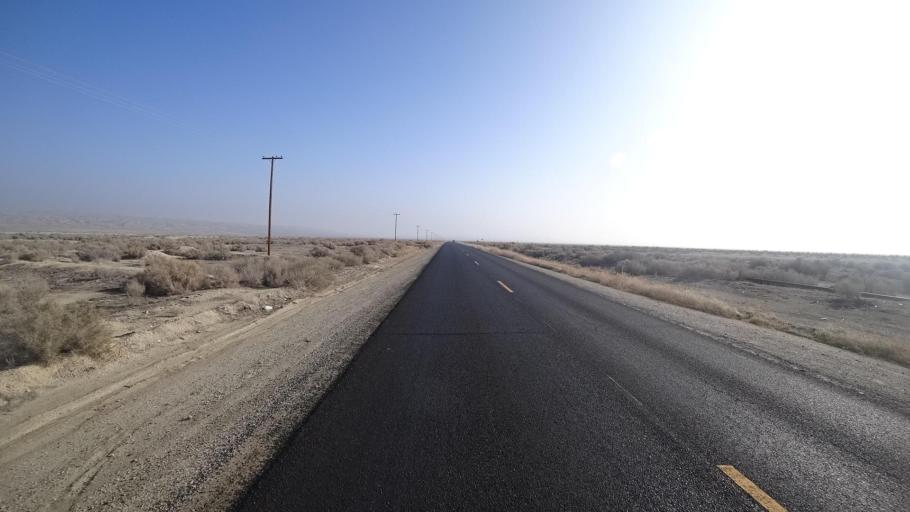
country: US
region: California
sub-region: Kern County
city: Taft Heights
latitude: 35.1805
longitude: -119.5103
